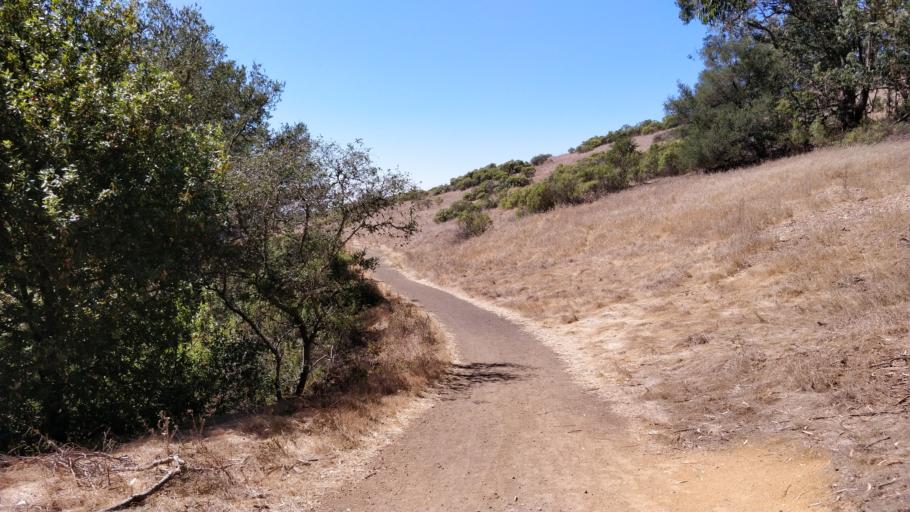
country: US
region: California
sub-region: Contra Costa County
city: Kensington
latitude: 37.9042
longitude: -122.2475
